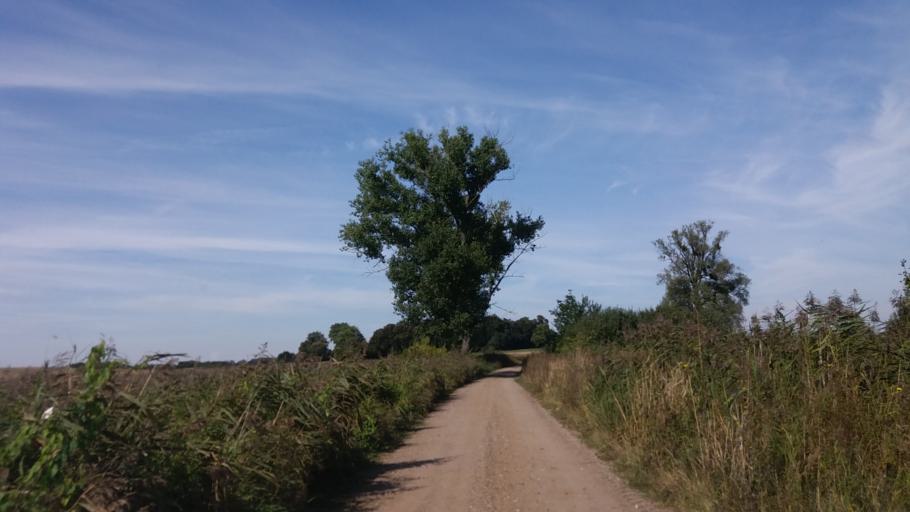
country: PL
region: West Pomeranian Voivodeship
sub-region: Powiat choszczenski
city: Choszczno
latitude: 53.1410
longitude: 15.4038
